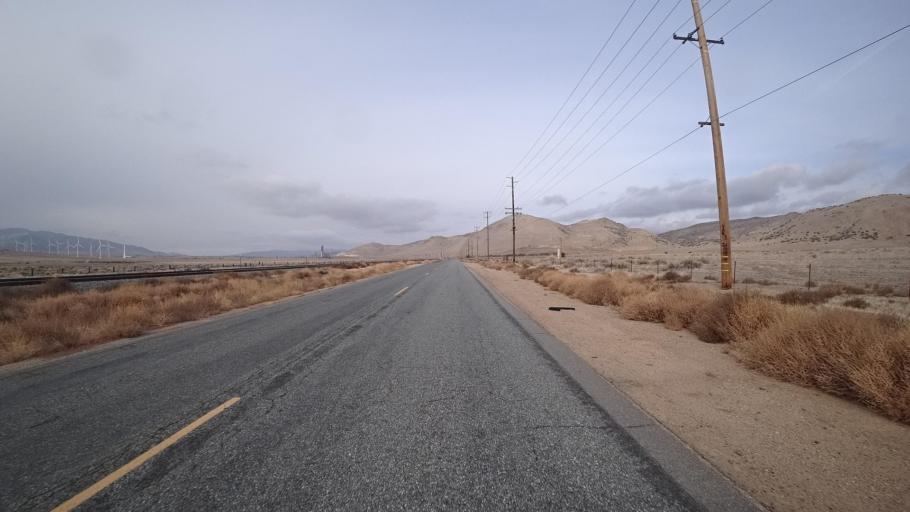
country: US
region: California
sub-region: Kern County
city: Tehachapi
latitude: 35.1164
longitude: -118.3313
